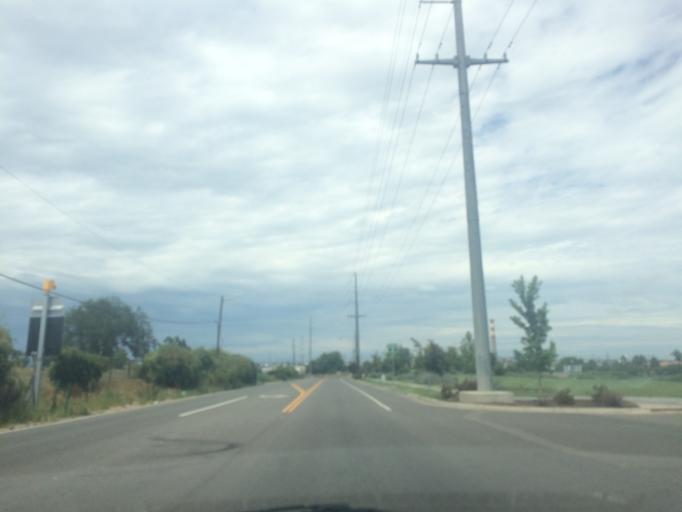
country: US
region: Colorado
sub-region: Adams County
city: Commerce City
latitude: 39.7955
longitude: -104.9578
